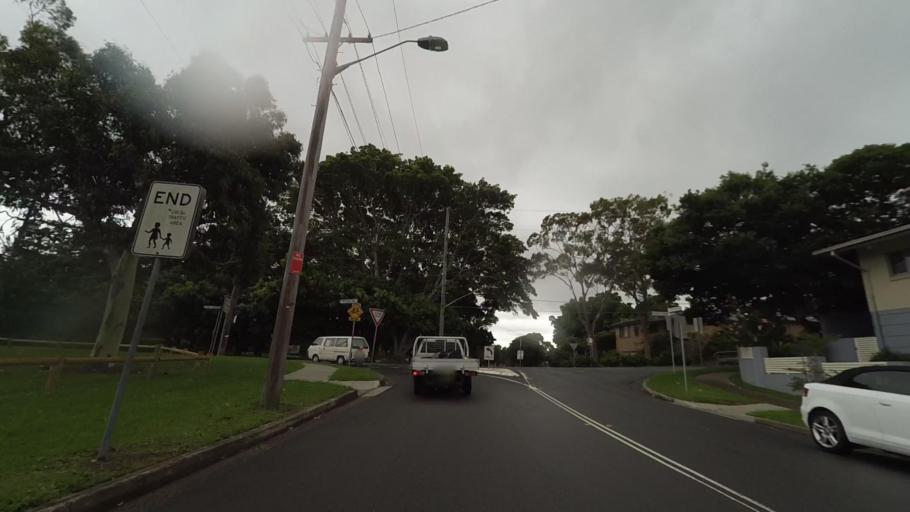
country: AU
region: New South Wales
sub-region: Kogarah
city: Beverly Park
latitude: -33.9840
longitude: 151.1328
